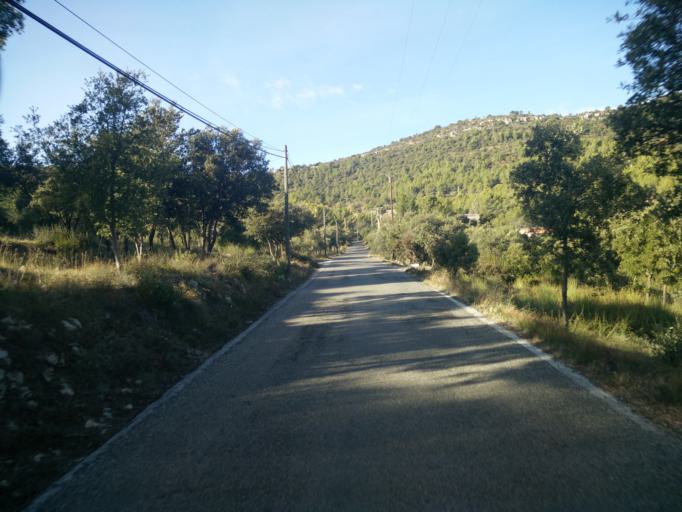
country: FR
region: Provence-Alpes-Cote d'Azur
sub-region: Departement du Var
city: Sollies-Toucas
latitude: 43.2051
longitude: 5.9963
